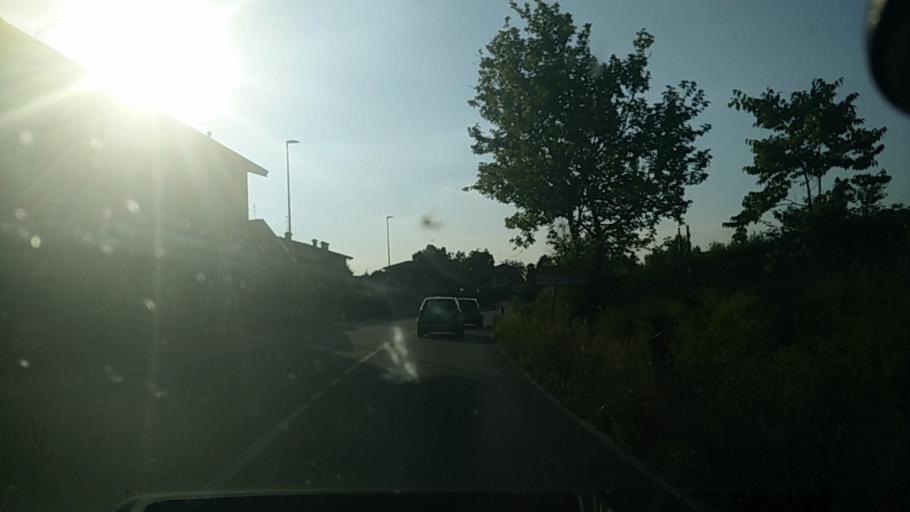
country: IT
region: Lombardy
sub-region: Provincia di Brescia
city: San Martino della Battaglia
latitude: 45.4508
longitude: 10.5875
